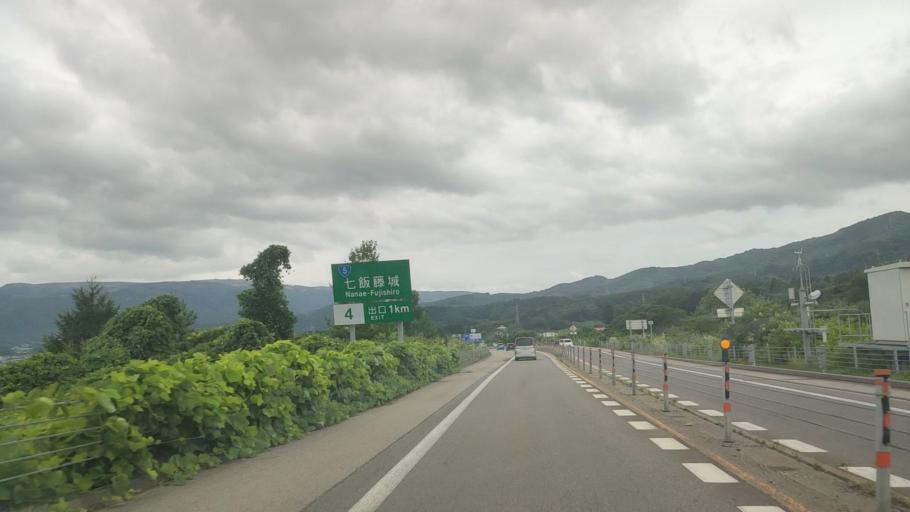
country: JP
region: Hokkaido
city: Nanae
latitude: 41.9182
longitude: 140.6821
